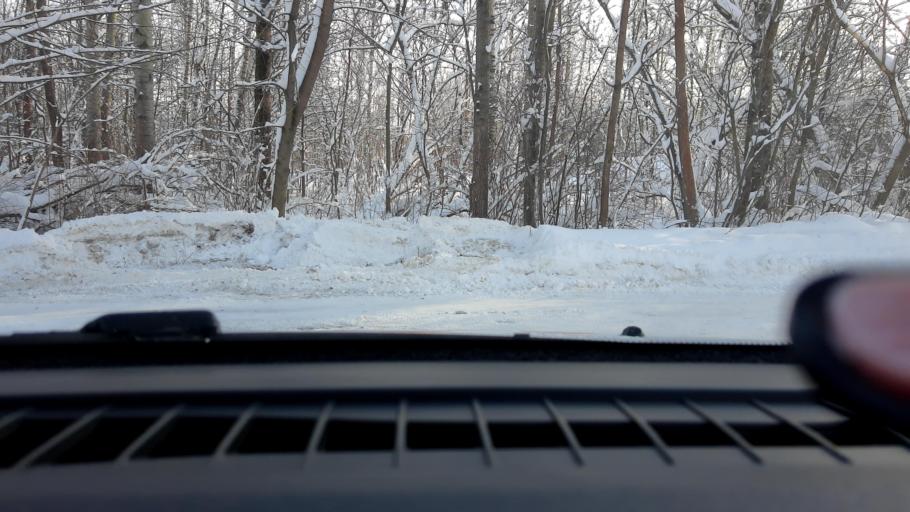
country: RU
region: Nizjnij Novgorod
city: Afonino
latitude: 56.1918
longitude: 44.0511
